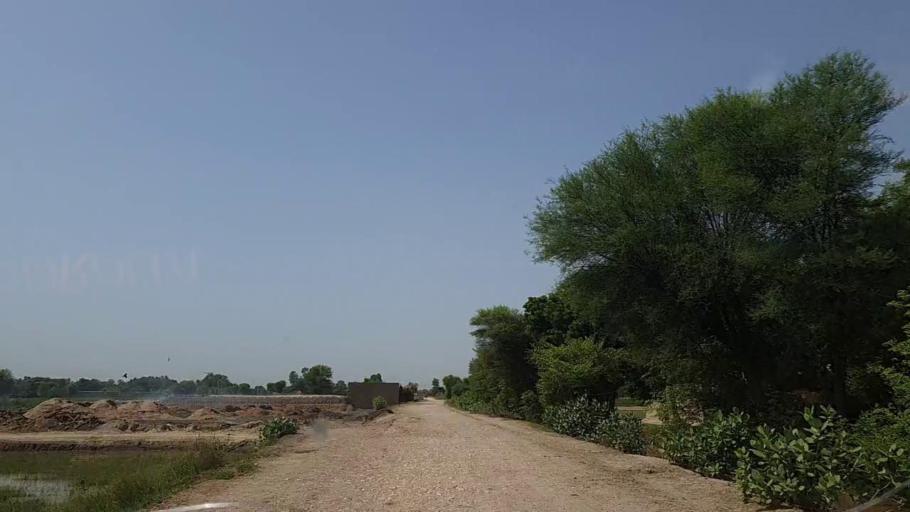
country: PK
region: Sindh
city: Naushahro Firoz
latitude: 26.8567
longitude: 68.0289
